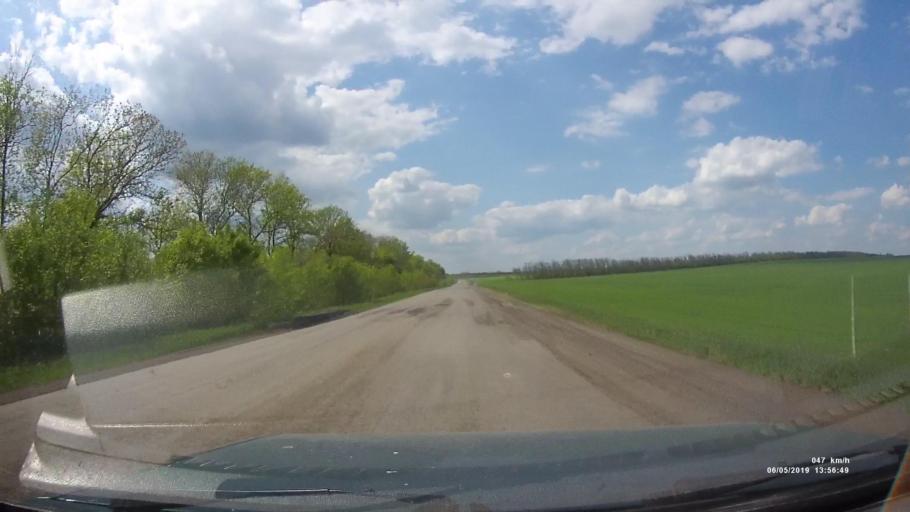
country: RU
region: Rostov
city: Melikhovskaya
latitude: 47.6825
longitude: 40.4278
